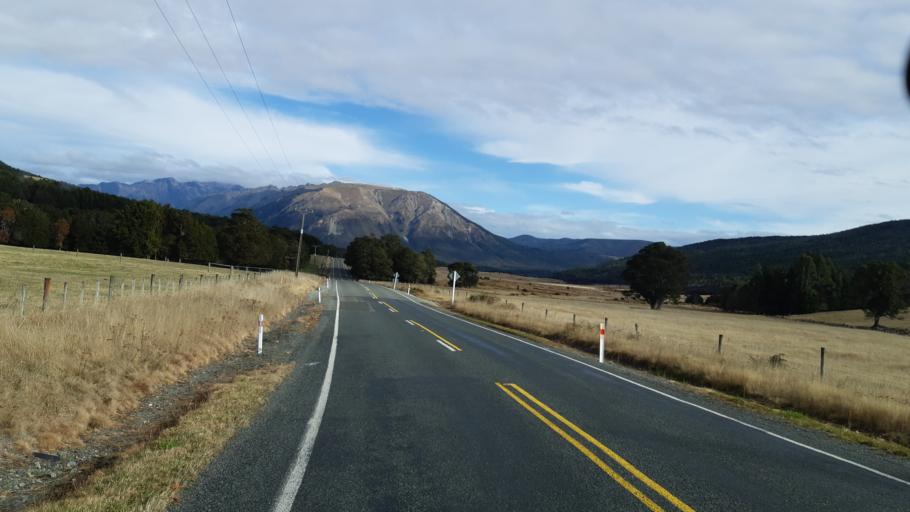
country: NZ
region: Tasman
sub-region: Tasman District
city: Wakefield
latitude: -41.7883
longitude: 172.8853
